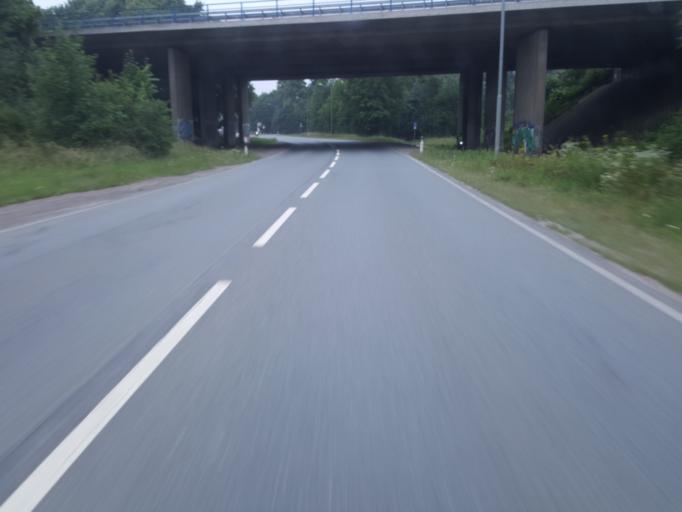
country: DE
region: North Rhine-Westphalia
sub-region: Regierungsbezirk Detmold
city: Kirchlengern
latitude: 52.1869
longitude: 8.6527
